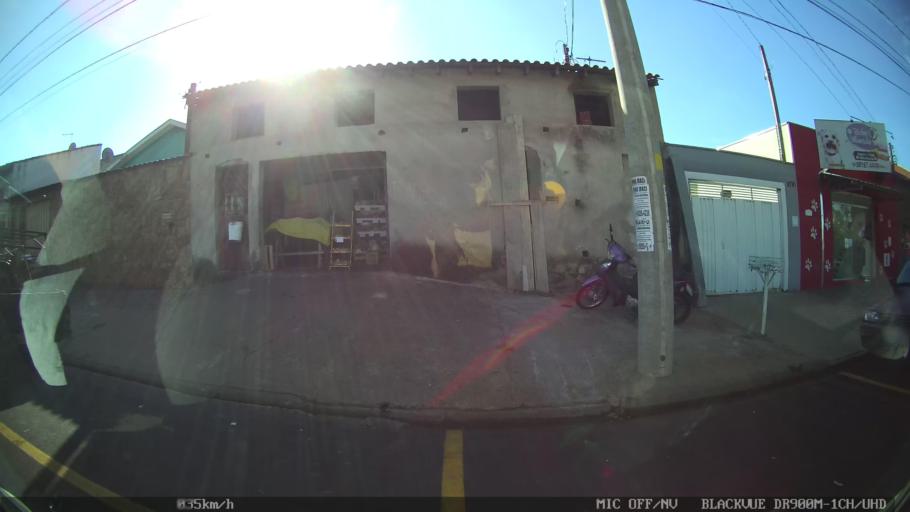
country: BR
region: Sao Paulo
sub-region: Franca
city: Franca
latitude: -20.5092
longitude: -47.4159
